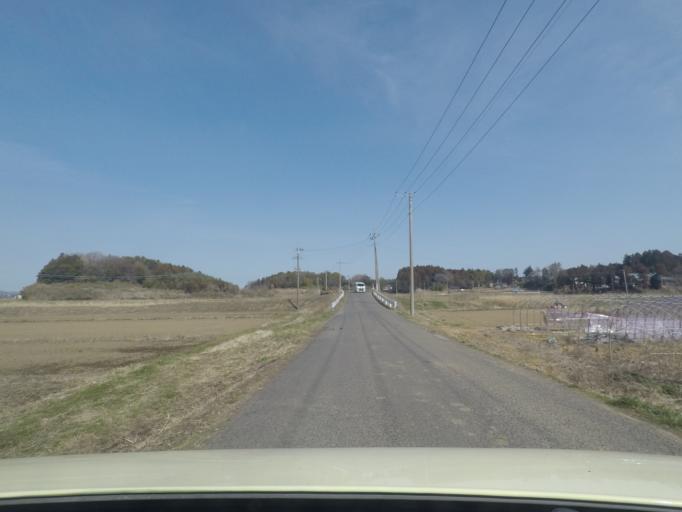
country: JP
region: Ibaraki
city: Ishioka
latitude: 36.2000
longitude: 140.3155
